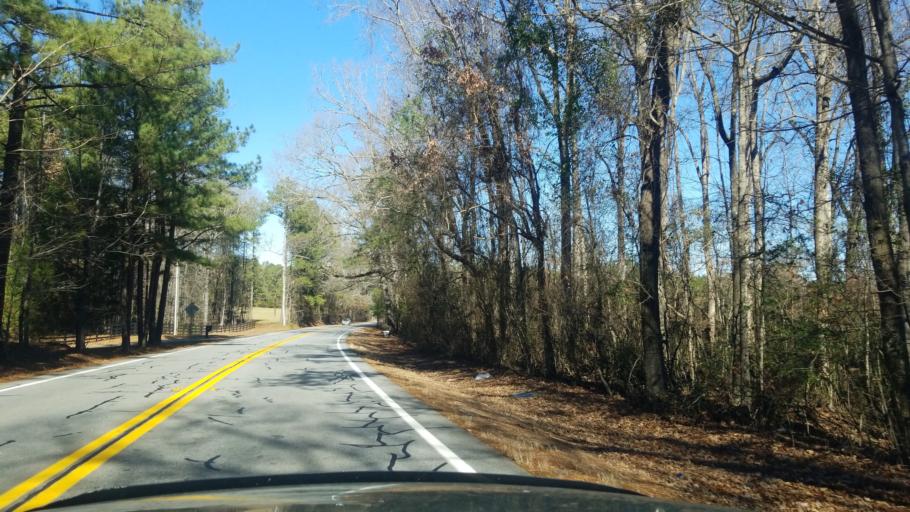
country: US
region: Georgia
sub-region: Harris County
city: Hamilton
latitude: 32.6759
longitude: -84.8592
